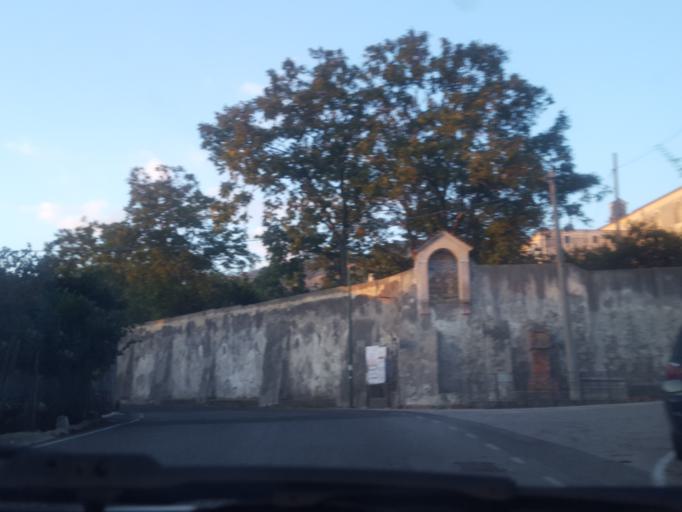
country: IT
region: Campania
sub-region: Provincia di Caserta
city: Arienzo
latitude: 41.0285
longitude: 14.4998
